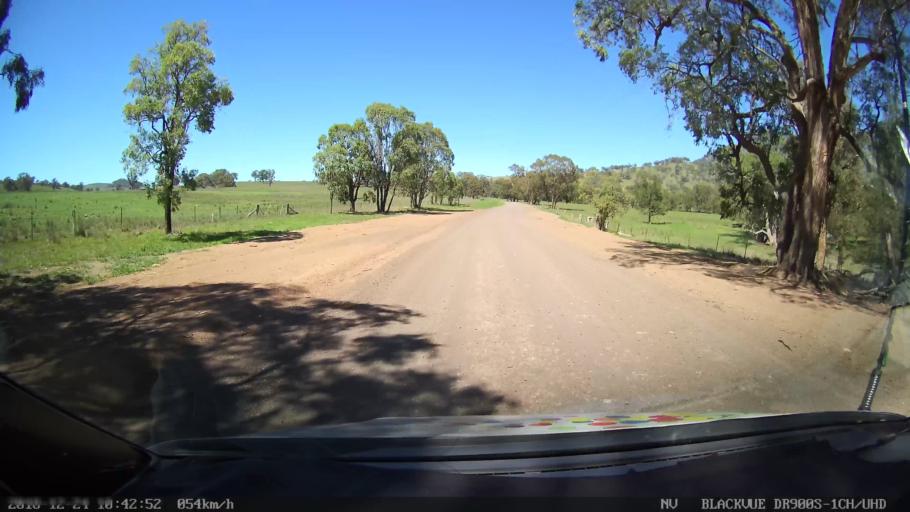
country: AU
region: New South Wales
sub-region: Upper Hunter Shire
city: Merriwa
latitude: -31.8790
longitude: 150.4501
